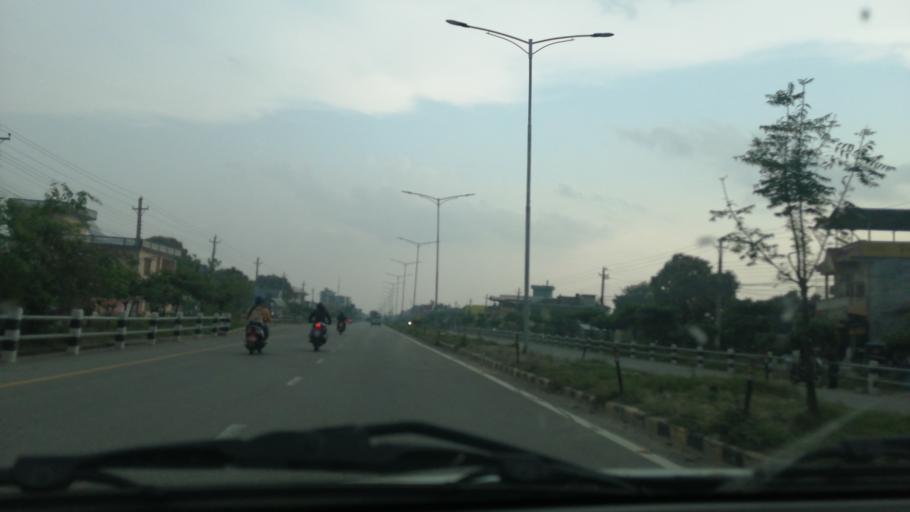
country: NP
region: Western Region
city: Butwal
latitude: 27.6368
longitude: 83.4717
